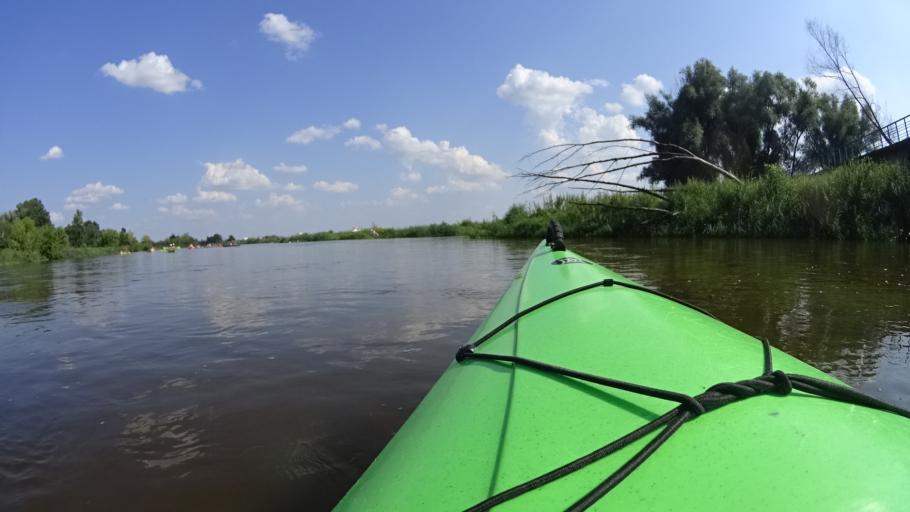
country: PL
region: Masovian Voivodeship
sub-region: Powiat bialobrzeski
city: Wysmierzyce
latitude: 51.6618
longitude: 20.8656
